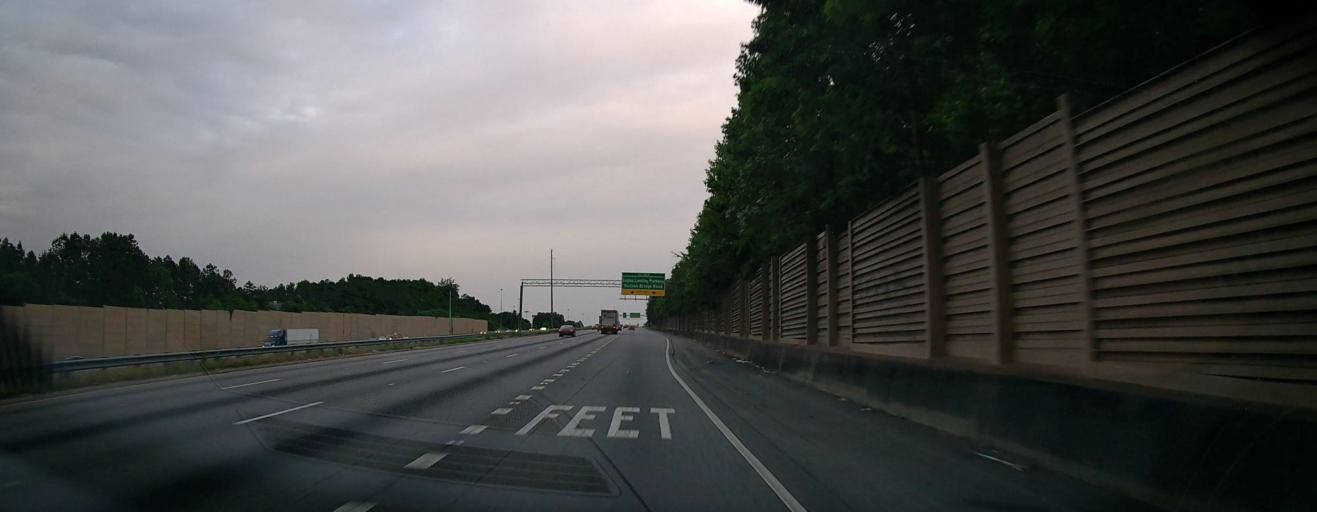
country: US
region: Georgia
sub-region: Henry County
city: Stockbridge
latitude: 33.5123
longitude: -84.2401
